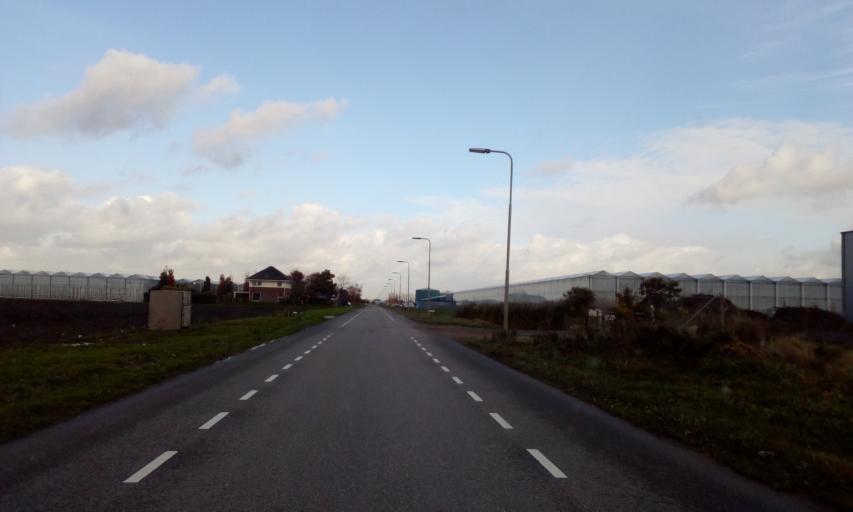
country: NL
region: South Holland
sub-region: Gemeente Lansingerland
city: Bleiswijk
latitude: 52.0103
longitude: 4.5150
